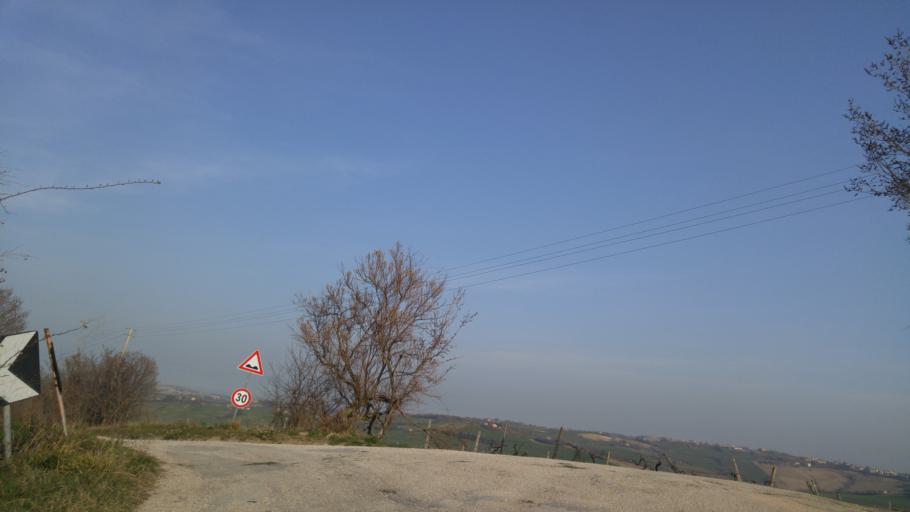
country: IT
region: The Marches
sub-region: Provincia di Pesaro e Urbino
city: Bellocchi
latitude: 43.7659
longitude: 12.9950
